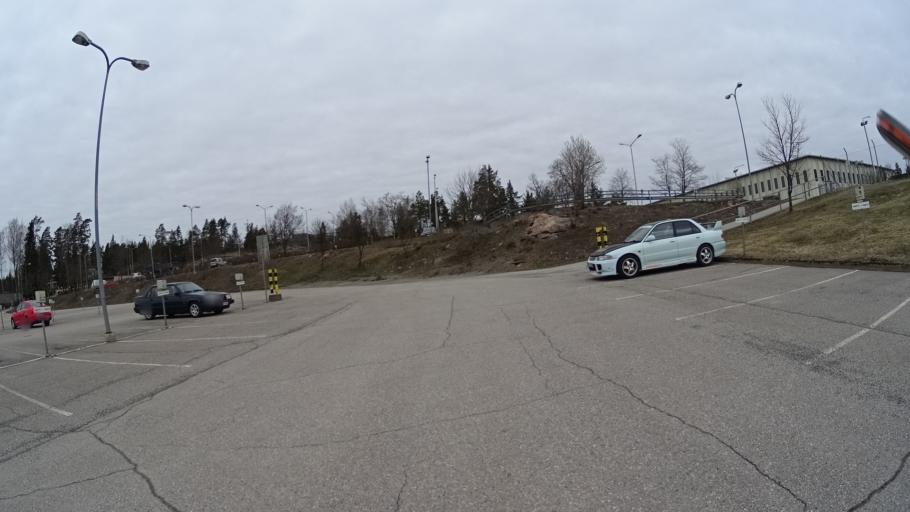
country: FI
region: Uusimaa
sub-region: Helsinki
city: Teekkarikylae
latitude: 60.3015
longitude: 24.8889
